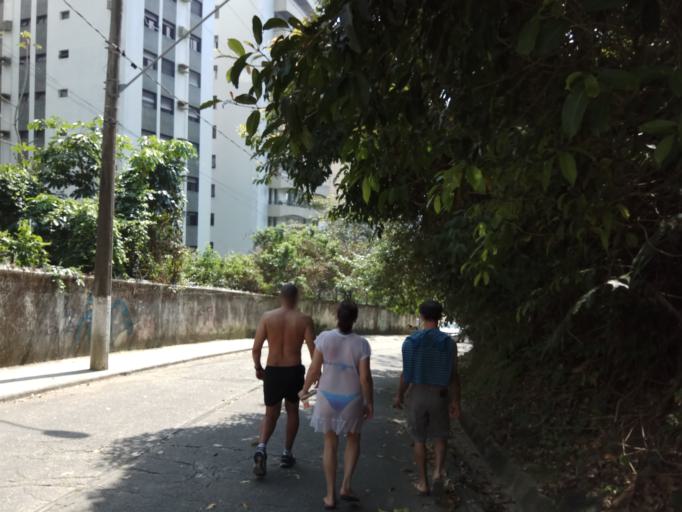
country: BR
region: Sao Paulo
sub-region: Guaruja
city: Guaruja
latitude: -23.9955
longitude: -46.2499
